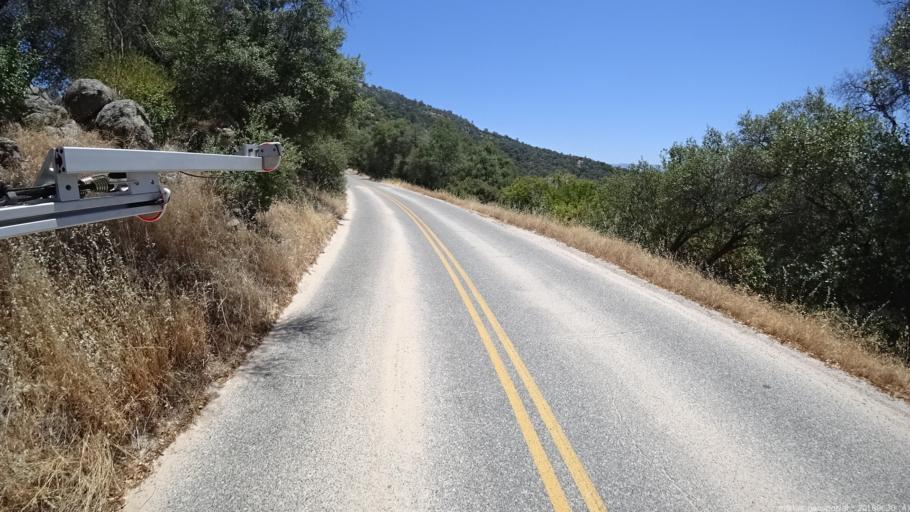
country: US
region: California
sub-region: Fresno County
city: Auberry
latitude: 37.1865
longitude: -119.4605
